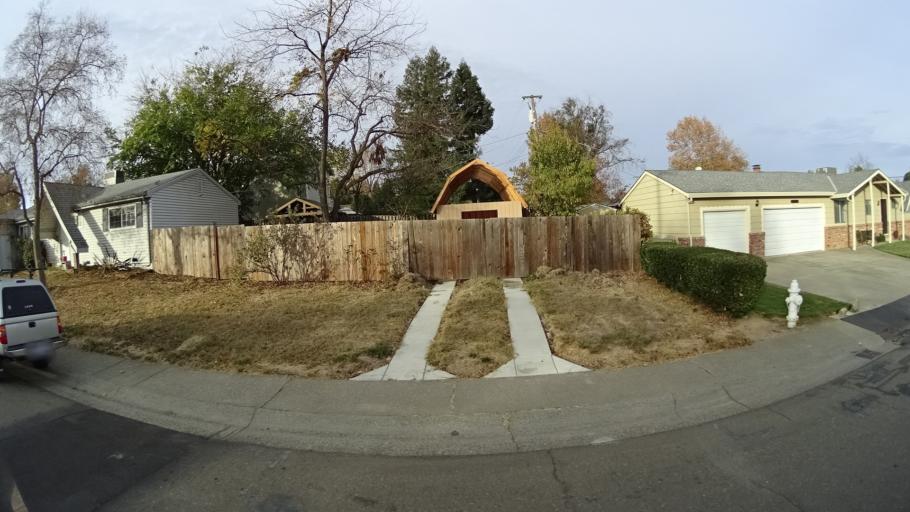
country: US
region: California
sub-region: Sacramento County
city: Citrus Heights
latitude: 38.7108
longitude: -121.2765
